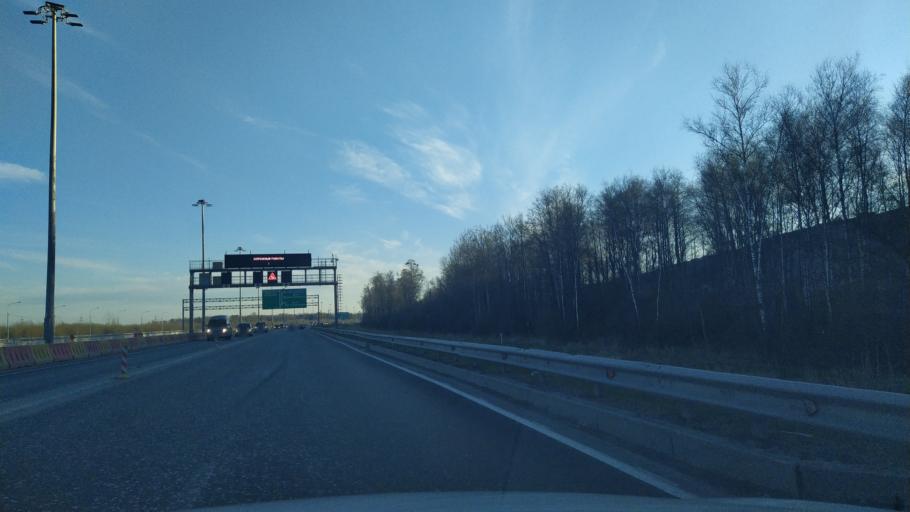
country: RU
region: St.-Petersburg
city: Levashovo
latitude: 60.0712
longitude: 30.1753
